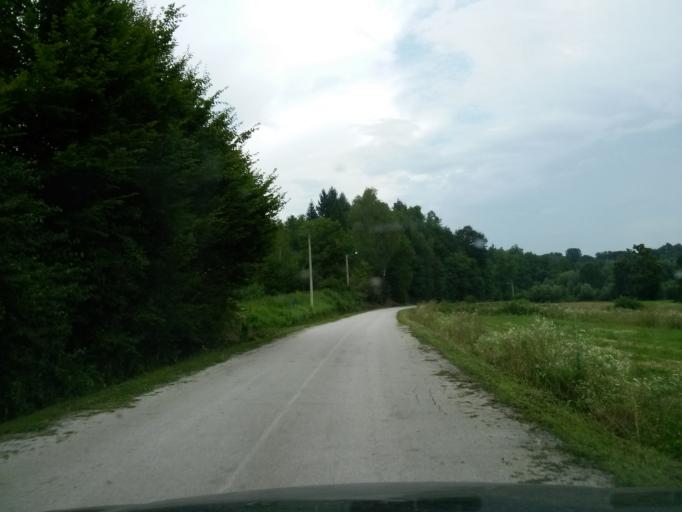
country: HR
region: Sisacko-Moslavacka
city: Glina
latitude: 45.3073
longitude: 15.9964
